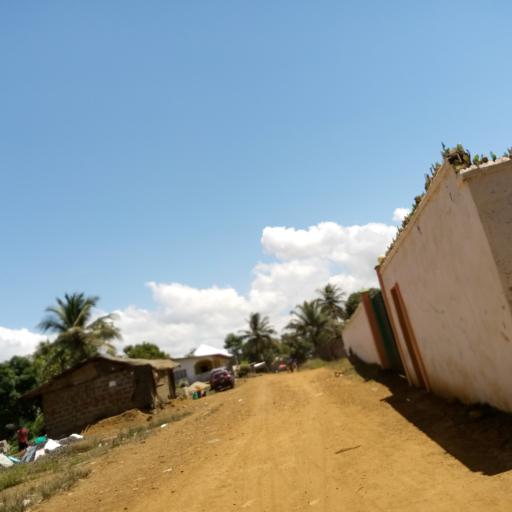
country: LR
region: Montserrado
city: Monrovia
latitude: 6.2500
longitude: -10.6899
